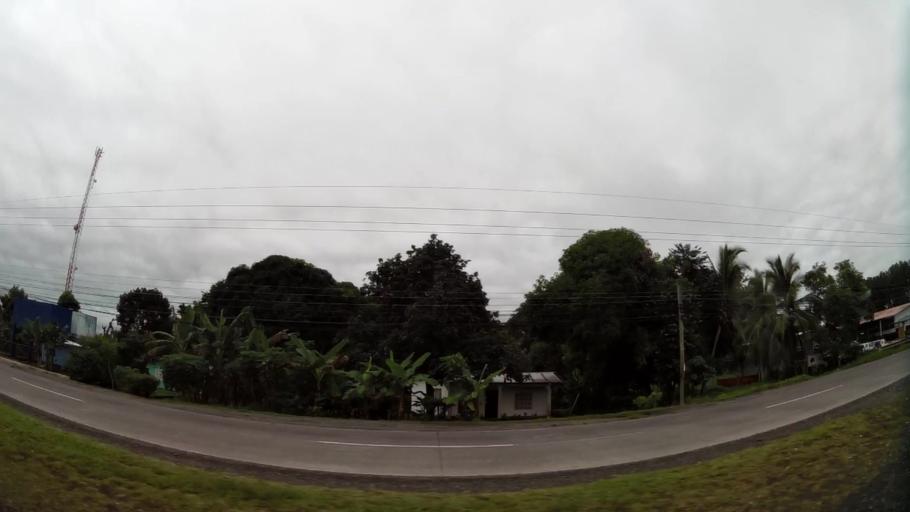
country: PA
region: Chiriqui
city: Boqueron
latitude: 8.4840
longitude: -82.5638
